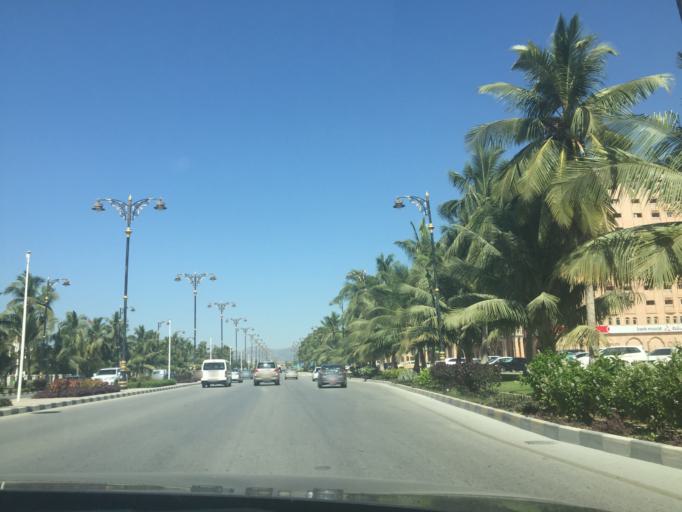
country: OM
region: Zufar
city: Salalah
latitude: 17.0197
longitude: 54.0921
